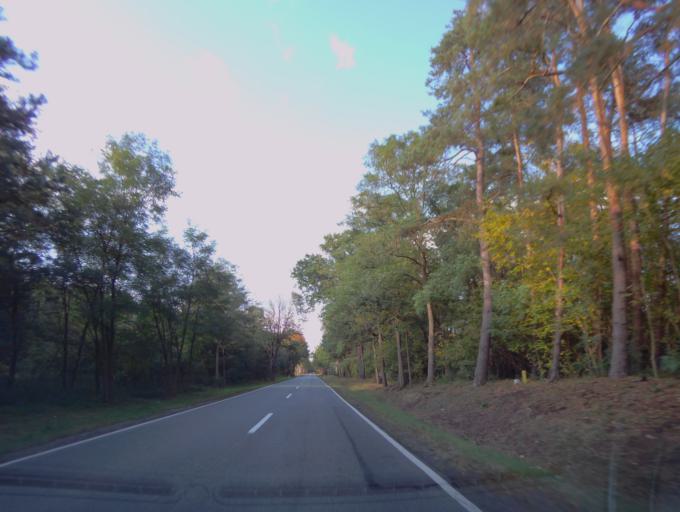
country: PL
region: Subcarpathian Voivodeship
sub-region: Powiat nizanski
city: Krzeszow
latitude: 50.3786
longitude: 22.3108
